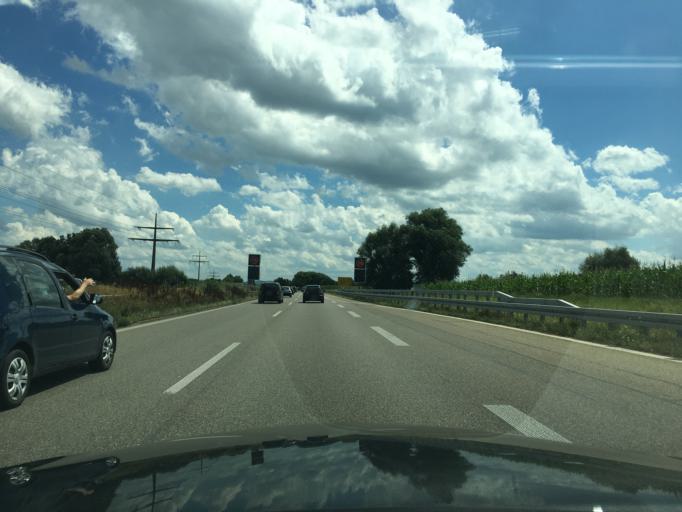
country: DE
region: Baden-Wuerttemberg
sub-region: Regierungsbezirk Stuttgart
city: Leinfelden-Echterdingen
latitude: 48.6735
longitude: 9.1874
